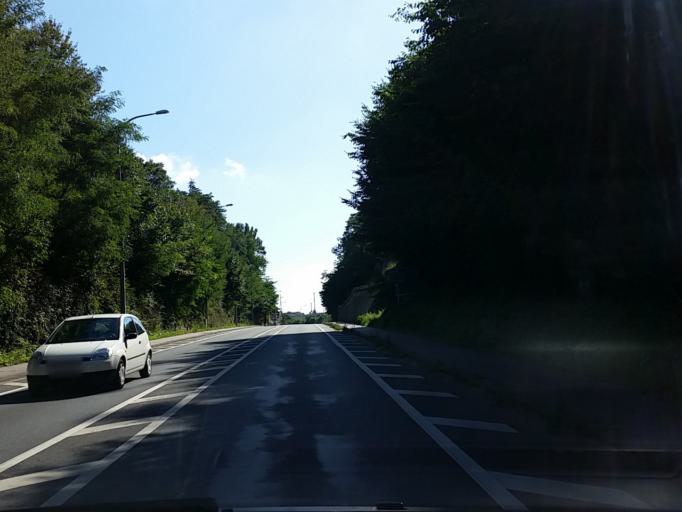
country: BE
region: Flanders
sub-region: Provincie Vlaams-Brabant
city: Herent
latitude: 50.8970
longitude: 4.6845
